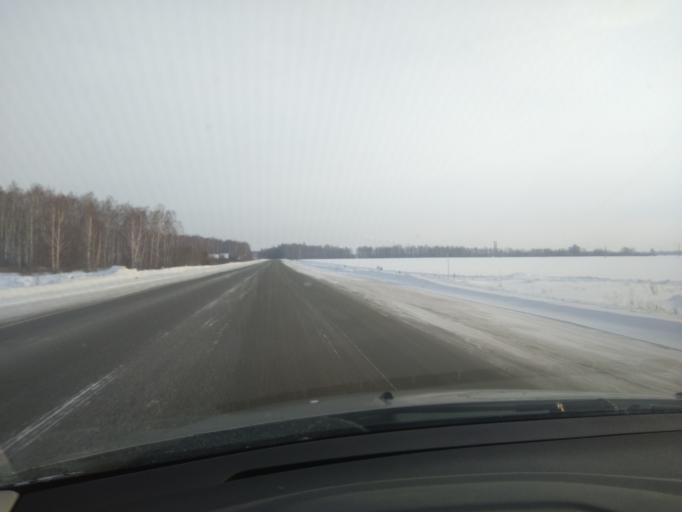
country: RU
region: Sverdlovsk
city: Bogdanovich
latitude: 56.7986
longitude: 62.0106
